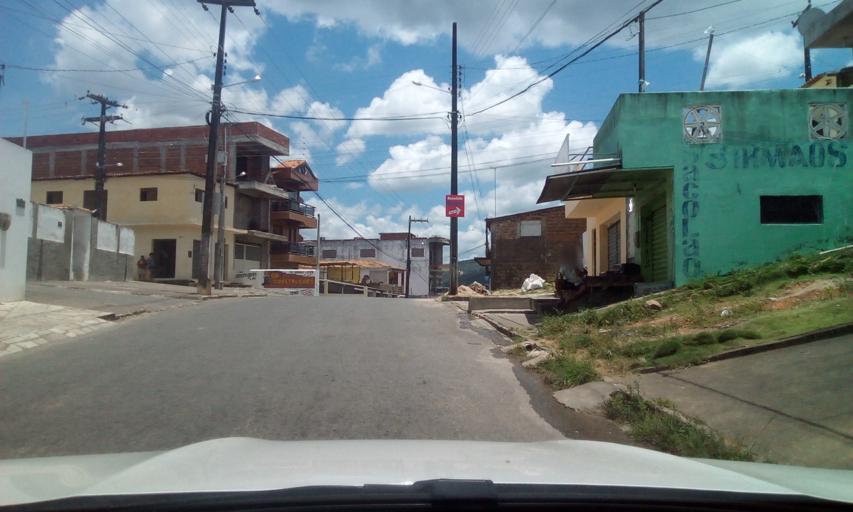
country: BR
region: Paraiba
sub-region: Guarabira
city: Guarabira
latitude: -6.8544
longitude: -35.4816
